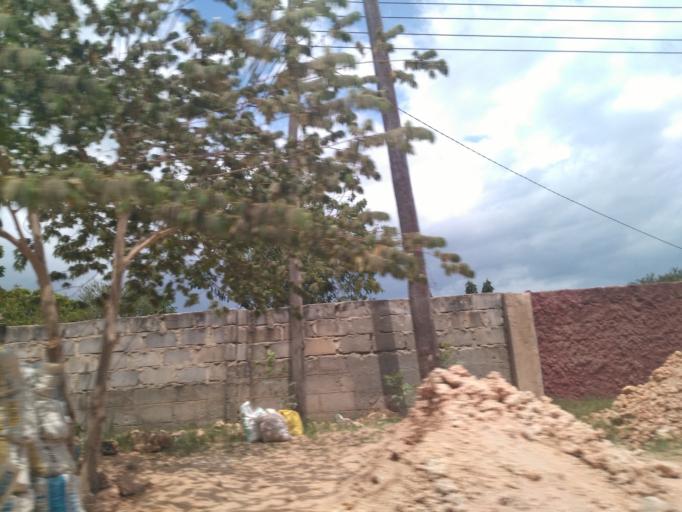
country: TZ
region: Dar es Salaam
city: Magomeni
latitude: -6.7606
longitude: 39.2730
